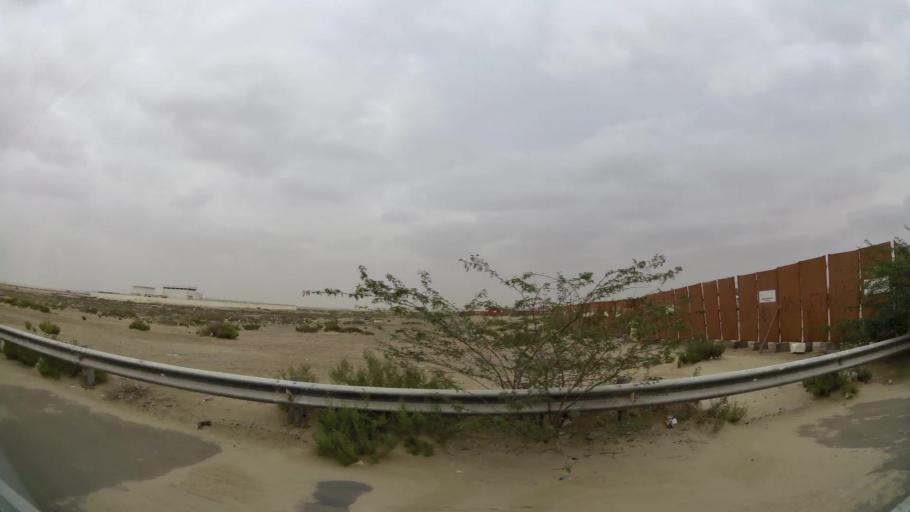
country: AE
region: Abu Dhabi
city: Abu Dhabi
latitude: 24.3235
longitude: 54.6422
